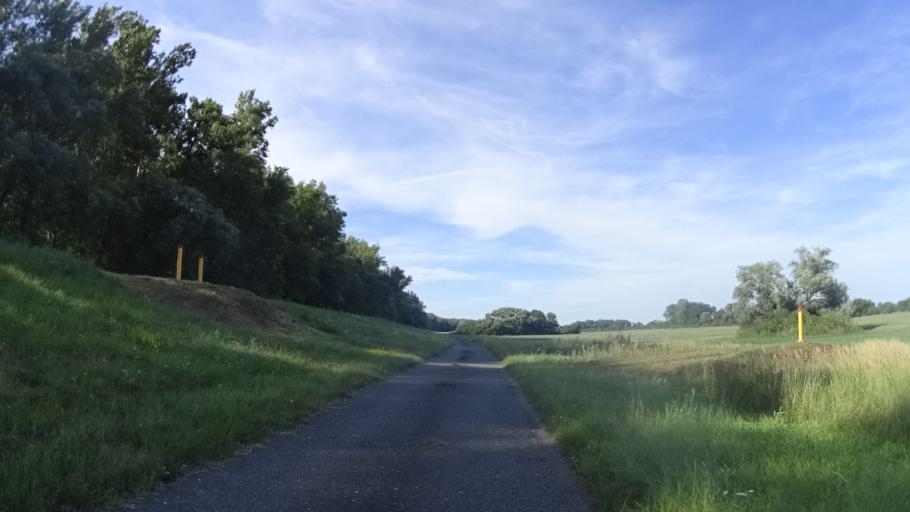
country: AT
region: Lower Austria
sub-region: Politischer Bezirk Ganserndorf
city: Drosing
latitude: 48.5294
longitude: 16.9562
